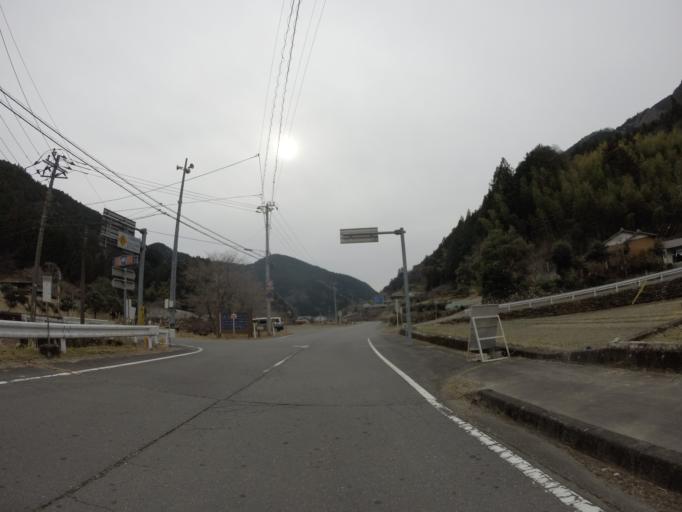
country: JP
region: Shizuoka
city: Fujinomiya
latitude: 35.2586
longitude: 138.5322
